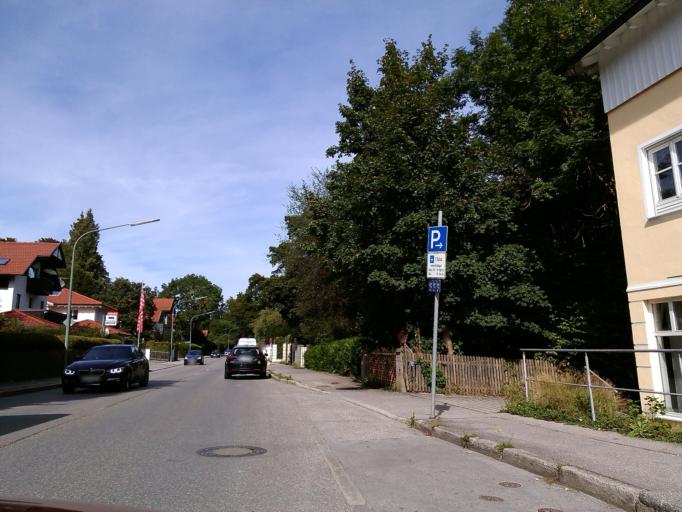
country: DE
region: Bavaria
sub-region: Upper Bavaria
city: Tutzing
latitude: 47.9121
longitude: 11.2816
